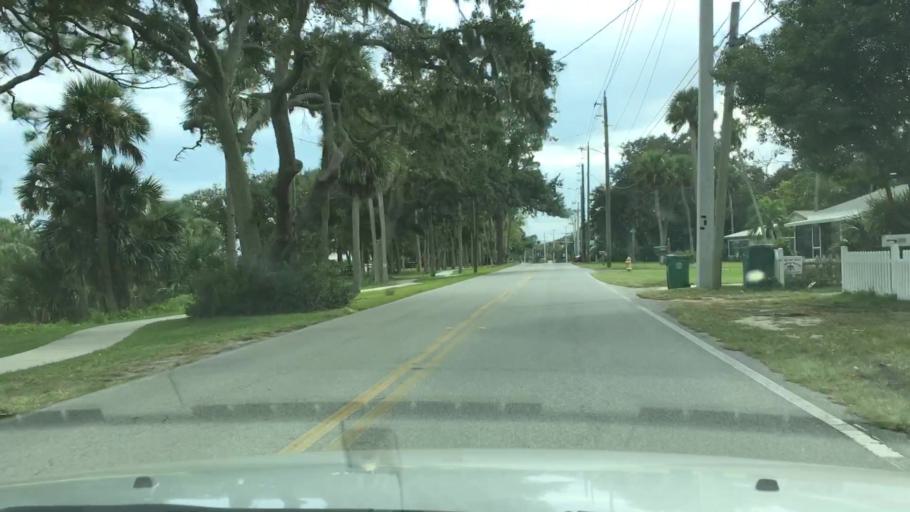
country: US
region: Florida
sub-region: Volusia County
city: Holly Hill
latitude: 29.2500
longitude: -81.0377
